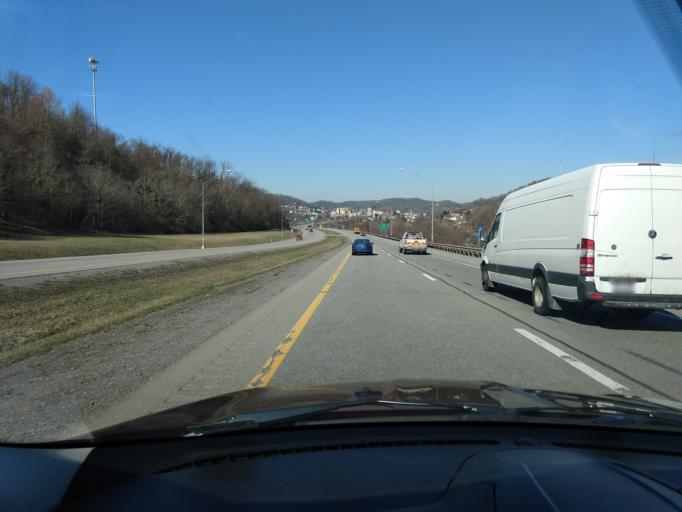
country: US
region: West Virginia
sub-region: Harrison County
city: Despard
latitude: 39.2772
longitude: -80.3100
